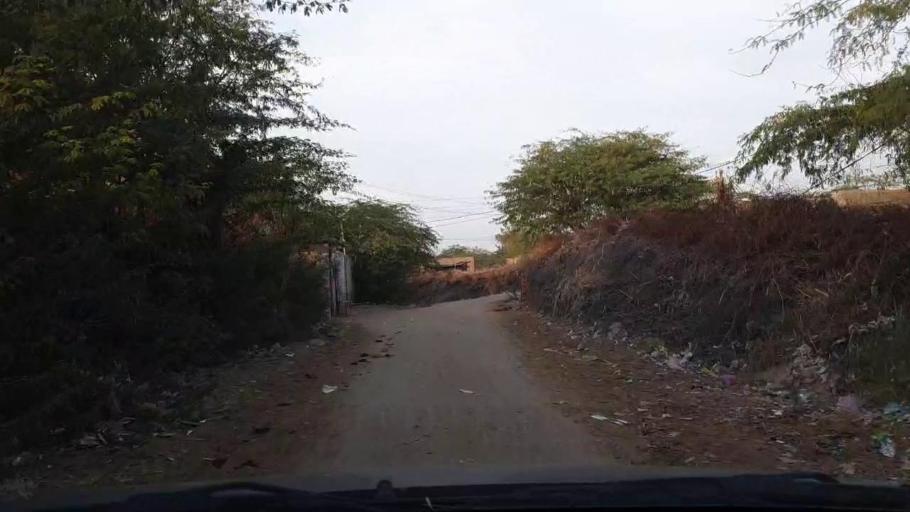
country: PK
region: Sindh
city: Khadro
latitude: 26.1382
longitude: 68.7454
